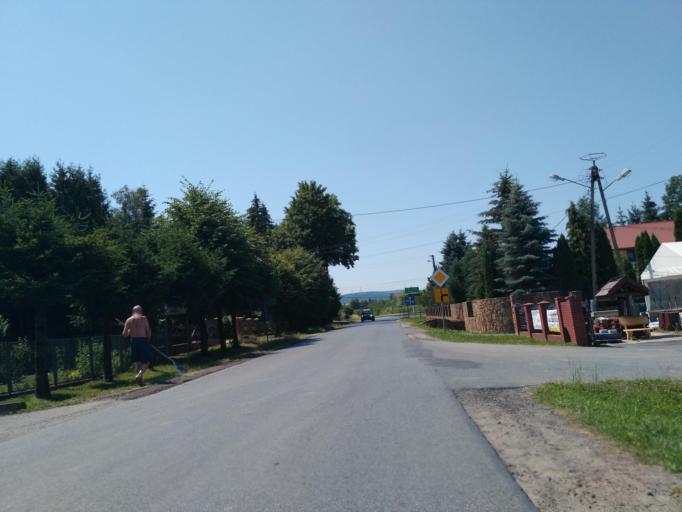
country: PL
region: Subcarpathian Voivodeship
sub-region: Powiat sanocki
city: Niebieszczany
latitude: 49.5390
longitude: 22.1306
